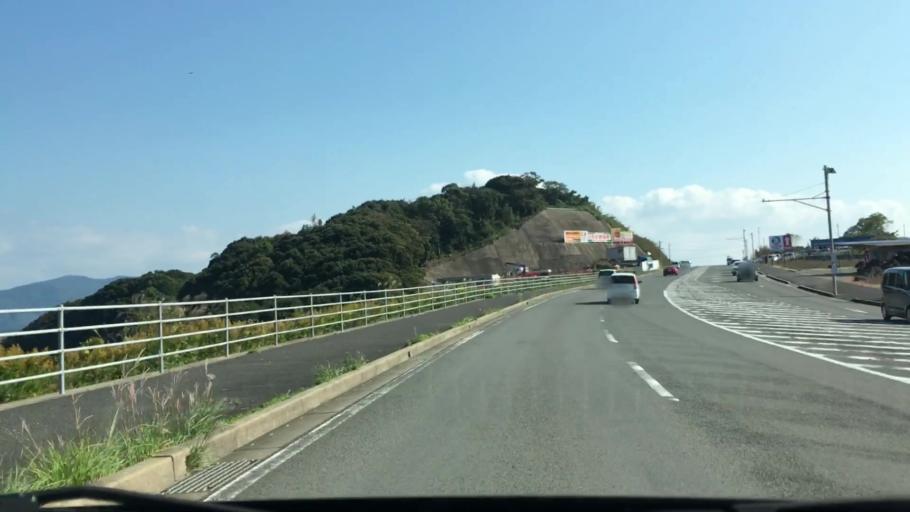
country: JP
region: Nagasaki
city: Togitsu
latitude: 32.8599
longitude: 129.8158
